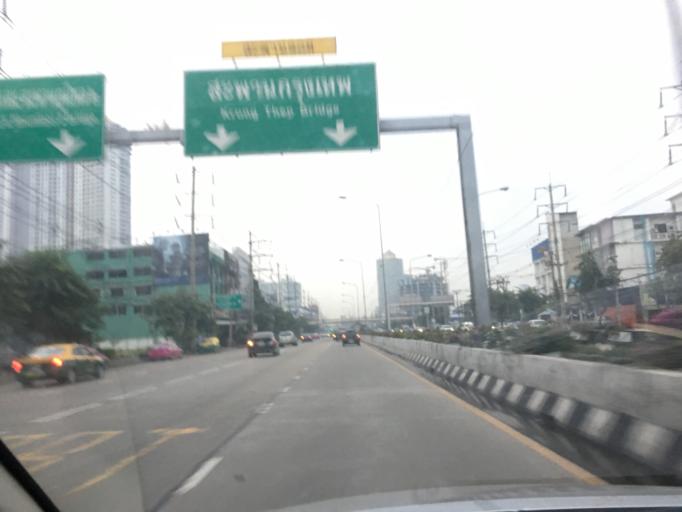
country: TH
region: Bangkok
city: Yan Nawa
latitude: 13.6920
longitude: 100.5475
